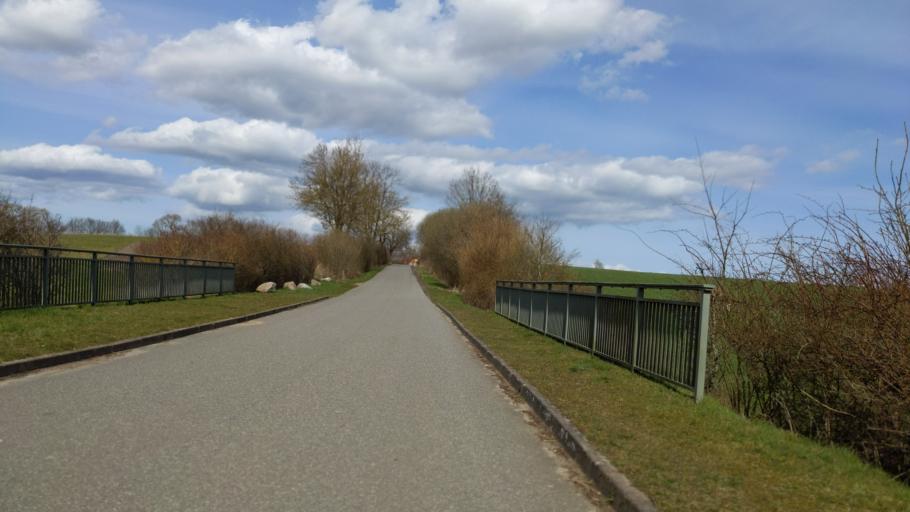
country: DE
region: Schleswig-Holstein
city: Susel
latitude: 54.0681
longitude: 10.6601
